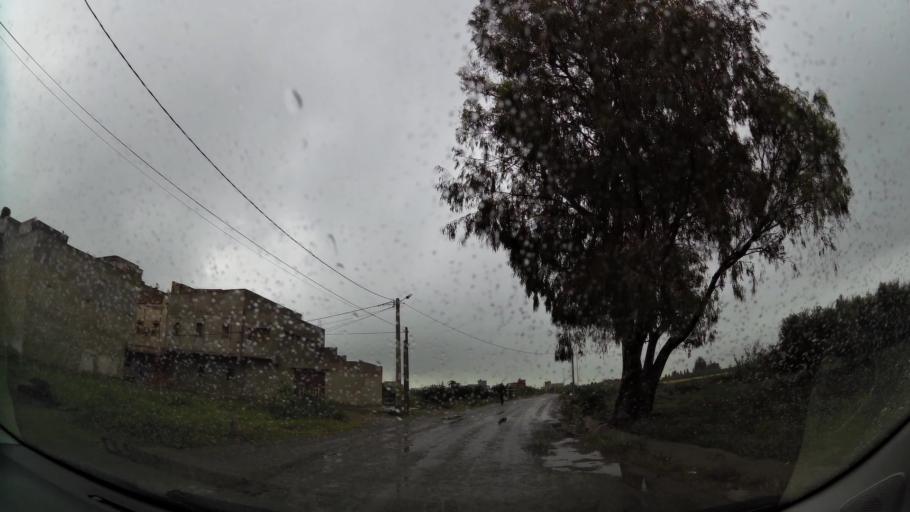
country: MA
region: Oriental
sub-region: Nador
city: Nador
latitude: 35.1535
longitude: -2.9734
